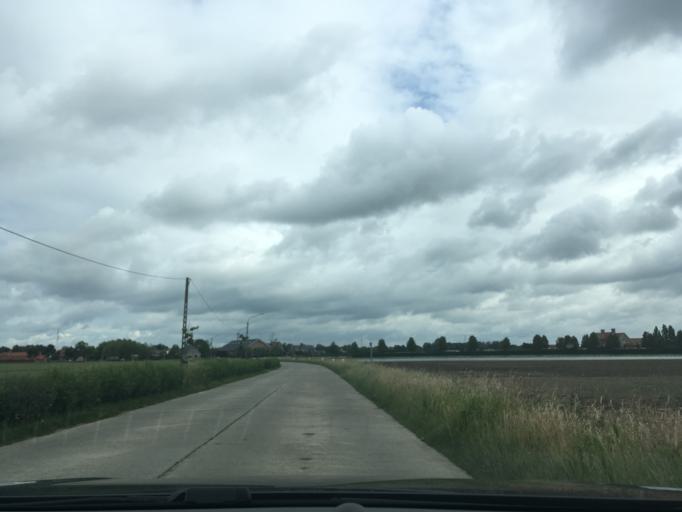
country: BE
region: Flanders
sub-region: Provincie West-Vlaanderen
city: Hooglede
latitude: 50.9489
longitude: 3.0601
